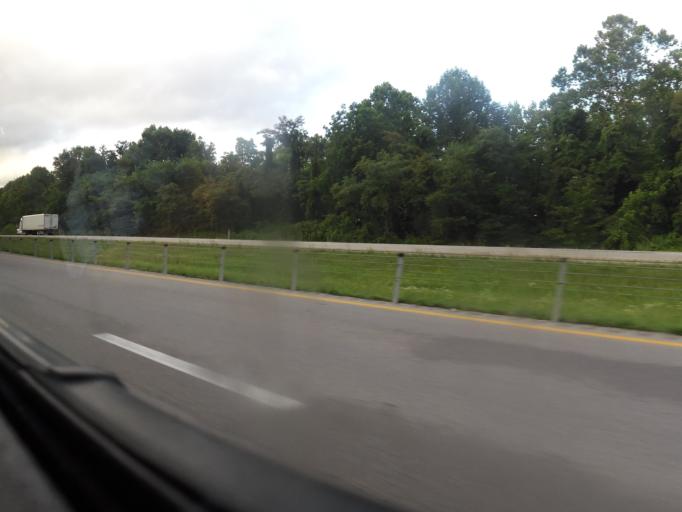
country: US
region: Kentucky
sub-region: Rockcastle County
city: Mount Vernon
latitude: 37.3112
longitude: -84.2910
